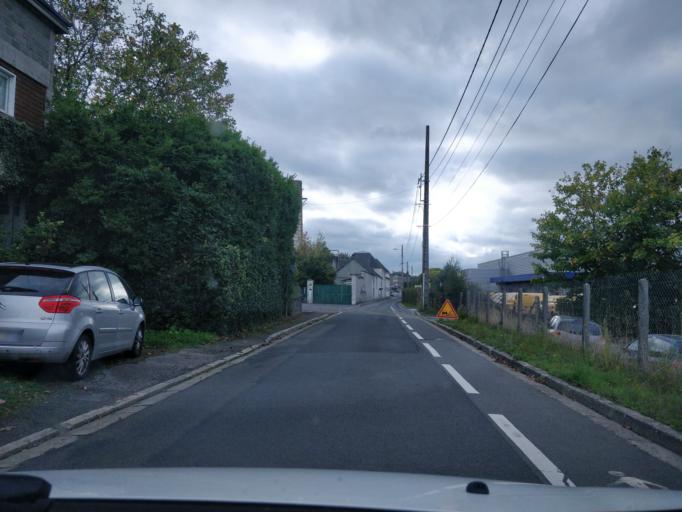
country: FR
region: Lower Normandy
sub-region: Departement du Calvados
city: Vire
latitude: 48.8466
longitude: -0.8795
